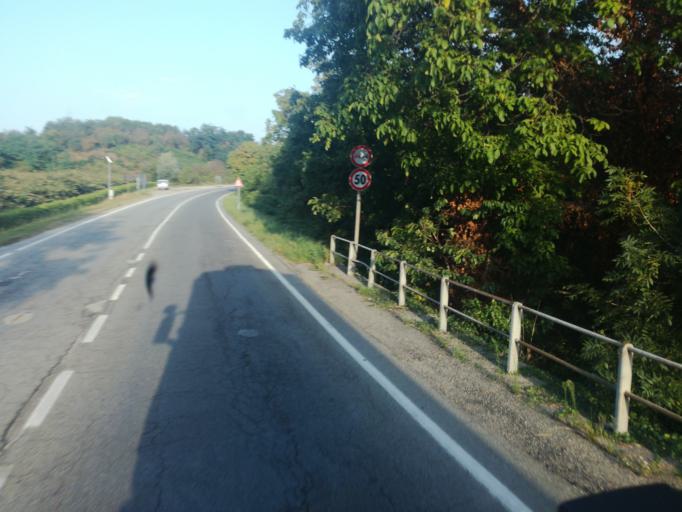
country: IT
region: Piedmont
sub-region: Provincia di Torino
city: Bibiana
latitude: 44.8101
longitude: 7.2821
